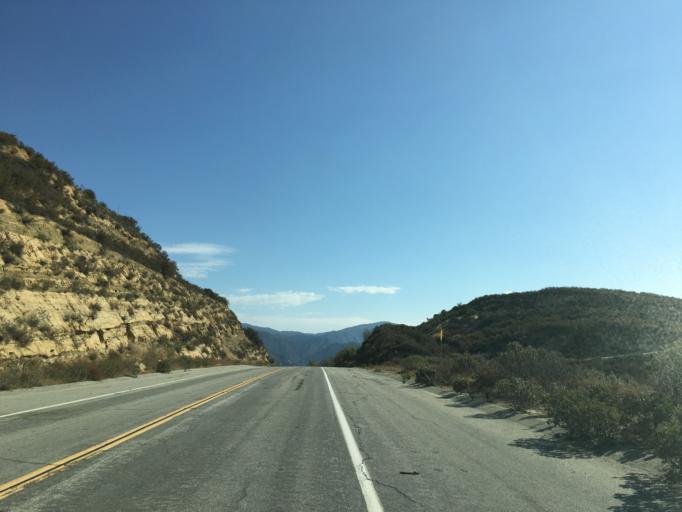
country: US
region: California
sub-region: Los Angeles County
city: Castaic
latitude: 34.5750
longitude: -118.6722
